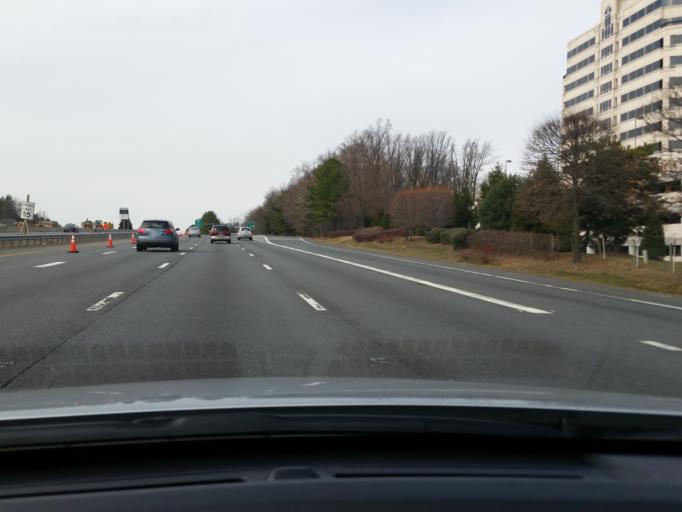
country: US
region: Virginia
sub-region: Fairfax County
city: Reston
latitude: 38.9511
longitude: -77.3495
